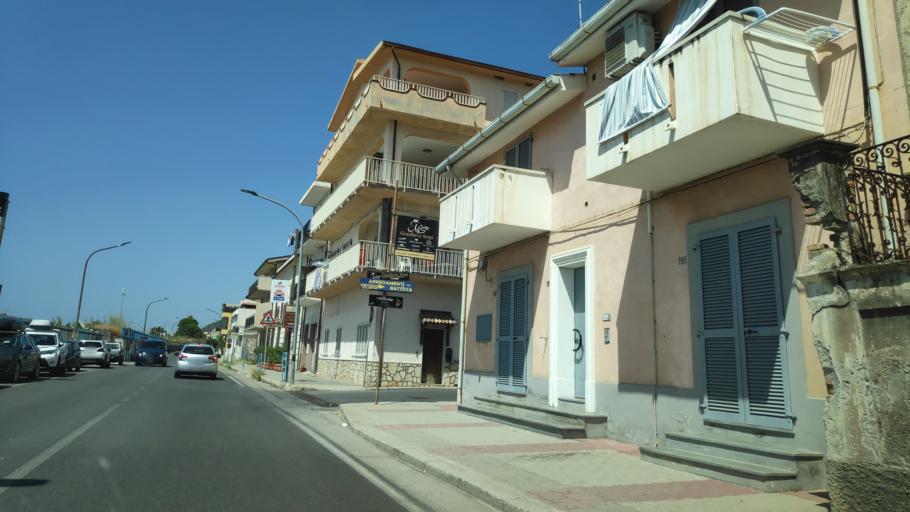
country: IT
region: Calabria
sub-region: Provincia di Reggio Calabria
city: Palizzi Marina
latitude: 37.9187
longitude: 15.9903
